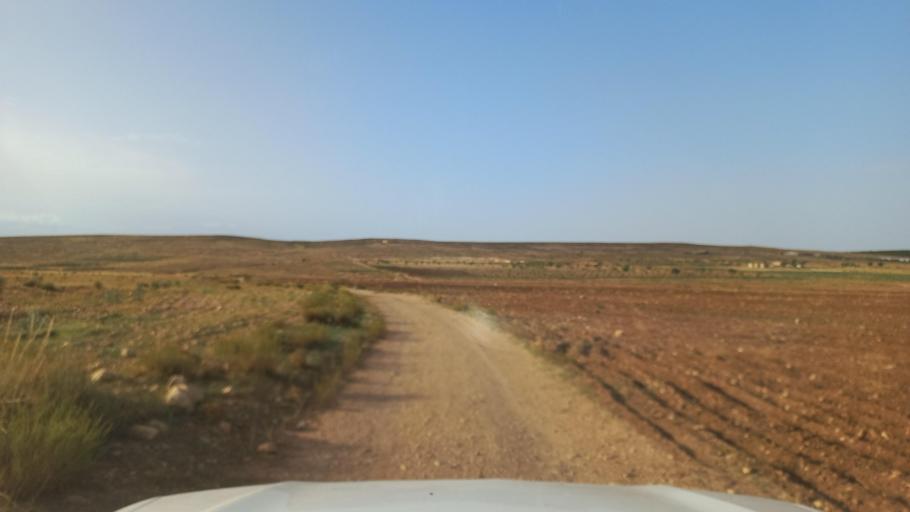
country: TN
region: Al Qasrayn
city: Kasserine
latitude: 35.3546
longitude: 8.8425
